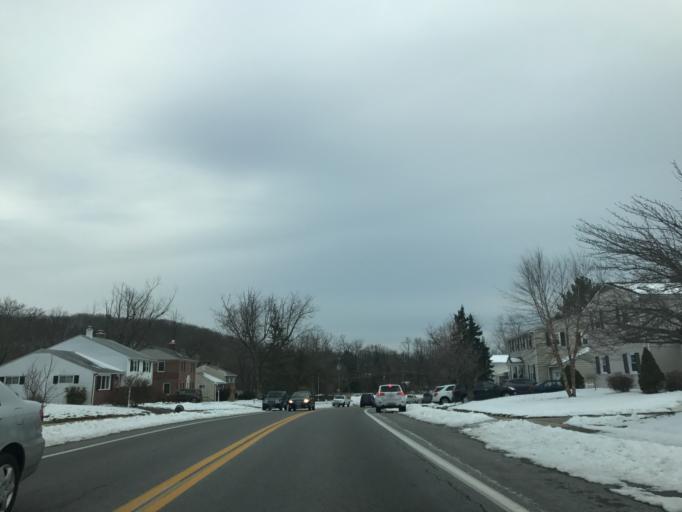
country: US
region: Maryland
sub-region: Baltimore County
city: Mays Chapel
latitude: 39.4166
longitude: -76.6471
